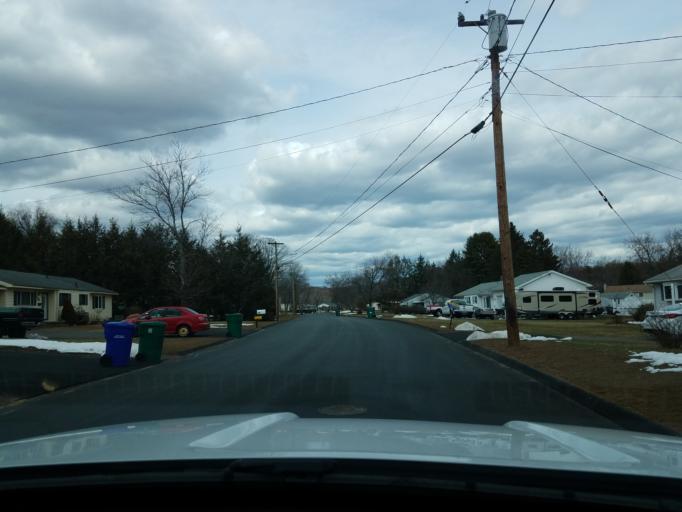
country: US
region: Connecticut
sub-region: Hartford County
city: Manchester
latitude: 41.8224
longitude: -72.5177
